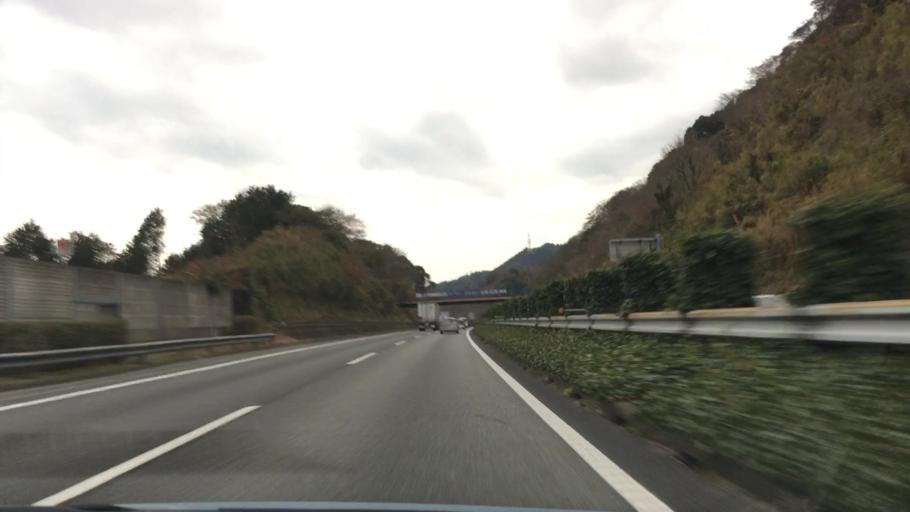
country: JP
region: Shizuoka
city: Fujinomiya
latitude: 35.1518
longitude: 138.6165
